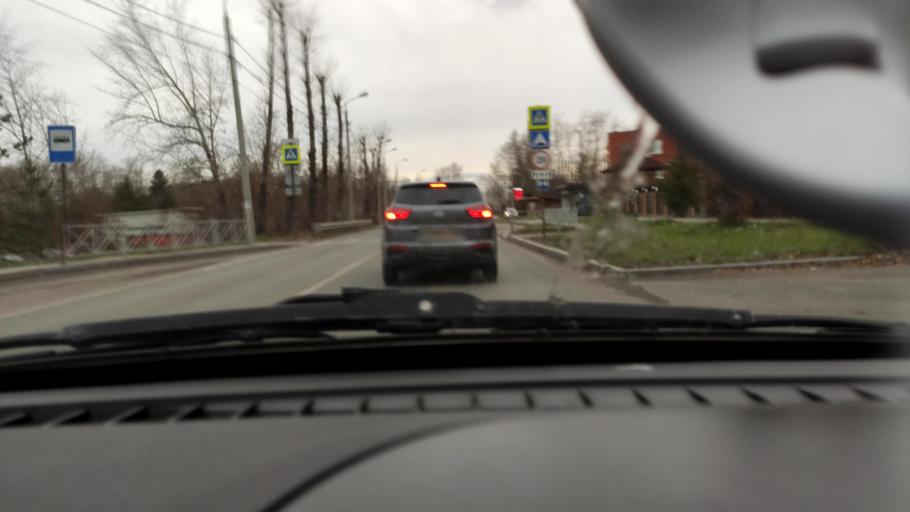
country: RU
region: Perm
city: Kondratovo
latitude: 57.9710
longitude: 56.1280
